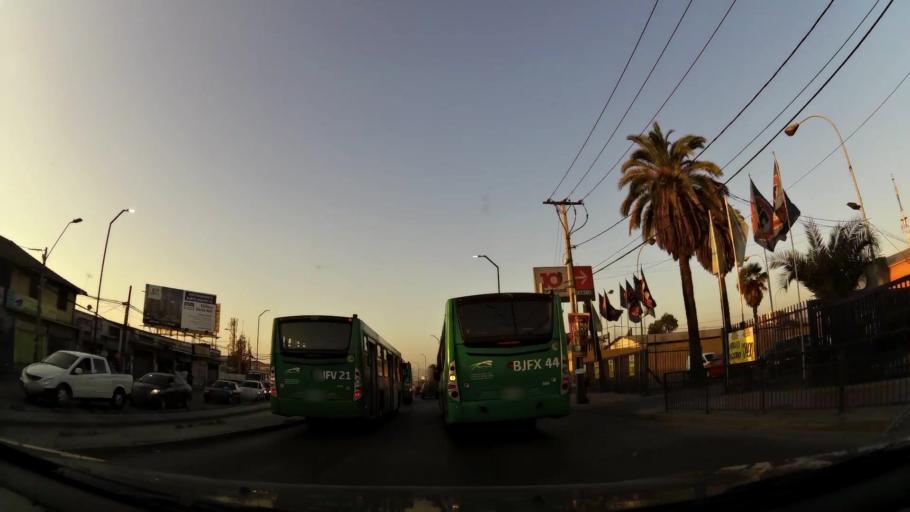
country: CL
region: Santiago Metropolitan
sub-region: Provincia de Santiago
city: La Pintana
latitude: -33.5421
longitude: -70.6654
